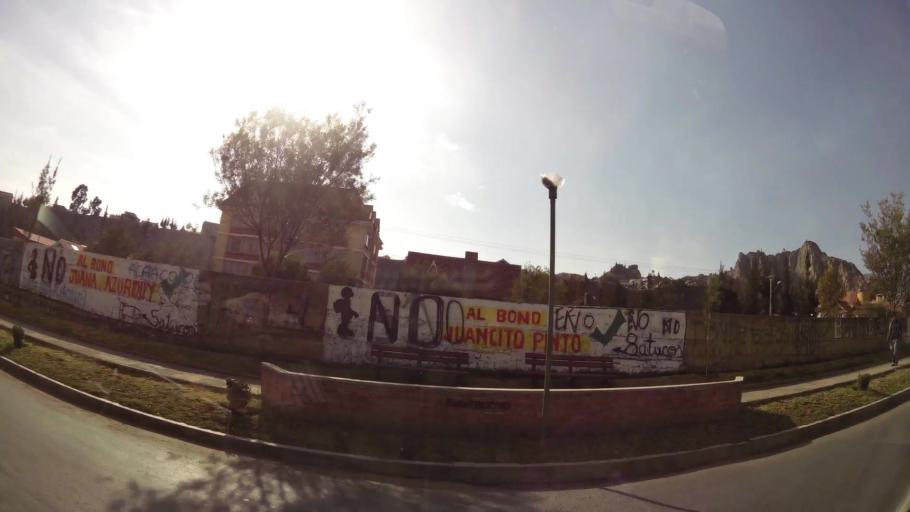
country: BO
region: La Paz
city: La Paz
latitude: -16.5293
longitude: -68.0727
